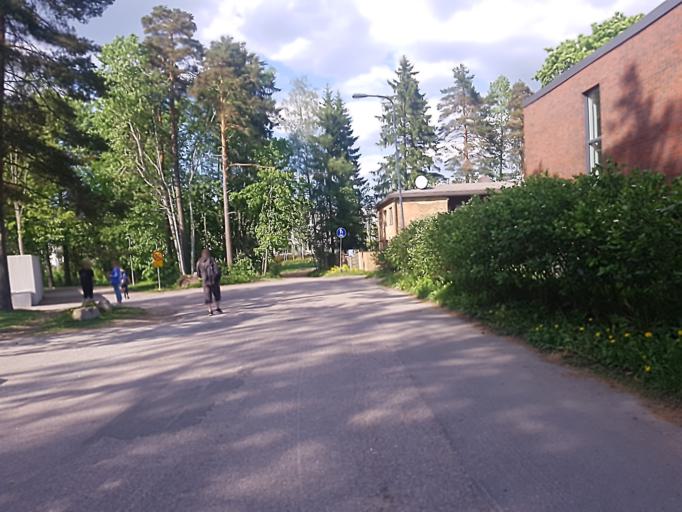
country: FI
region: Uusimaa
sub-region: Helsinki
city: Helsinki
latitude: 60.2205
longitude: 24.8997
